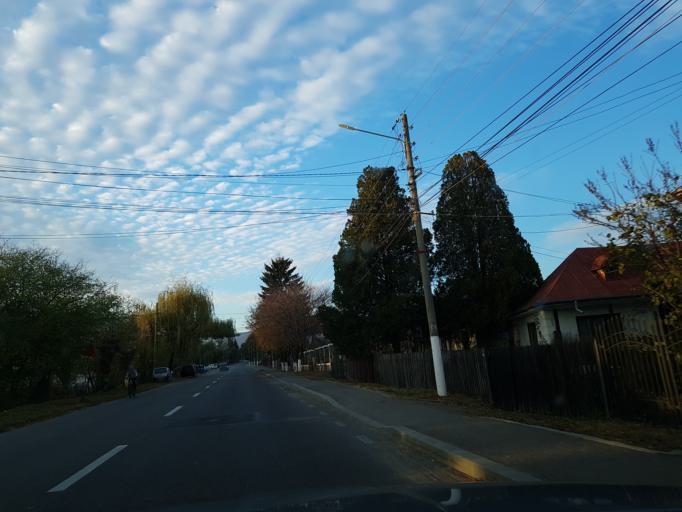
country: RO
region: Prahova
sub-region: Oras Breaza
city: Breaza de Sus
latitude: 45.1967
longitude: 25.6561
